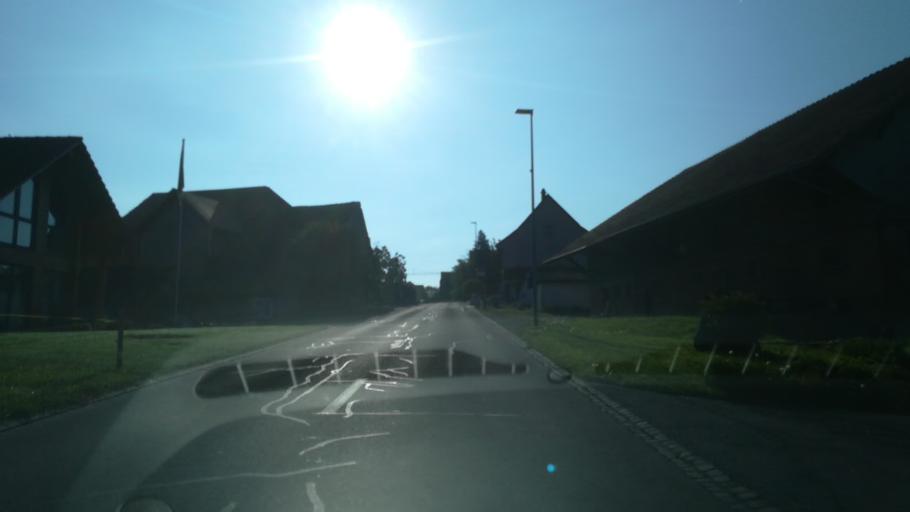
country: CH
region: Thurgau
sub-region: Frauenfeld District
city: Homburg
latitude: 47.6347
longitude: 8.9892
